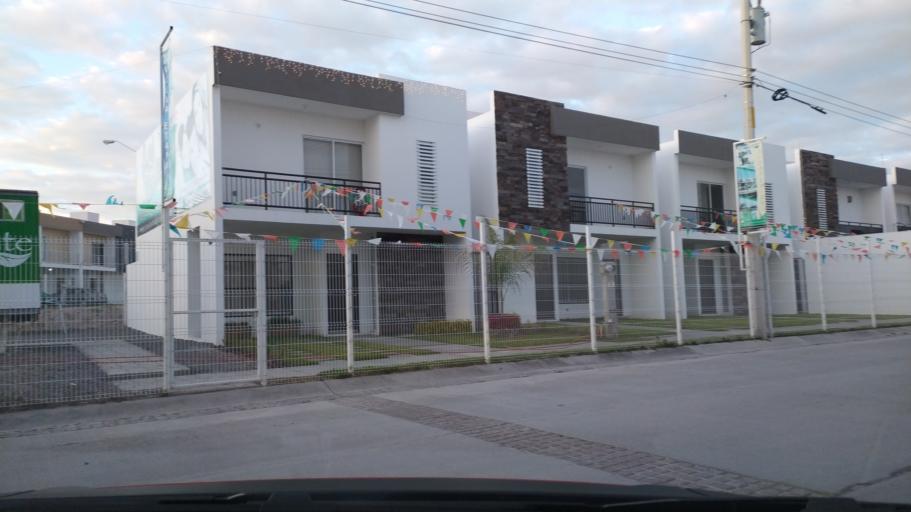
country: MX
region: Guanajuato
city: San Francisco del Rincon
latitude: 21.0336
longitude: -101.8477
